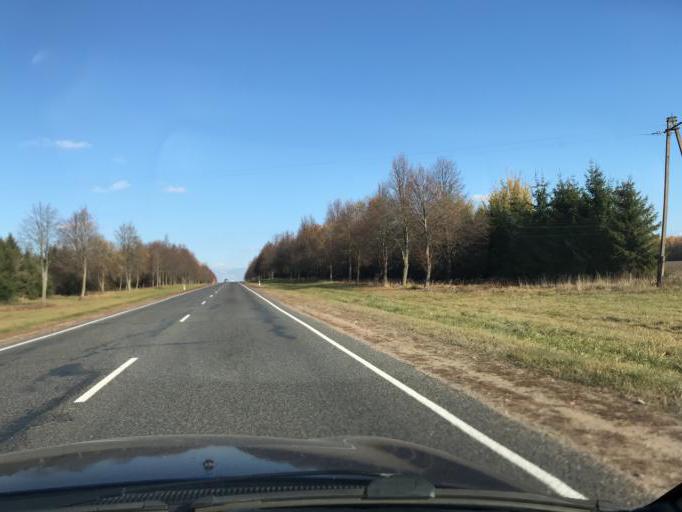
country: BY
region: Grodnenskaya
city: Lida
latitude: 53.9994
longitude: 25.2130
